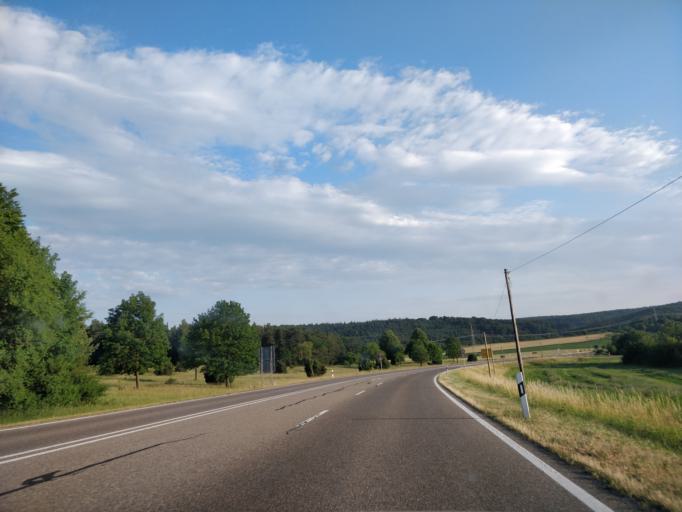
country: DE
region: Bavaria
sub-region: Swabia
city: Ederheim
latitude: 48.8150
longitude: 10.4562
